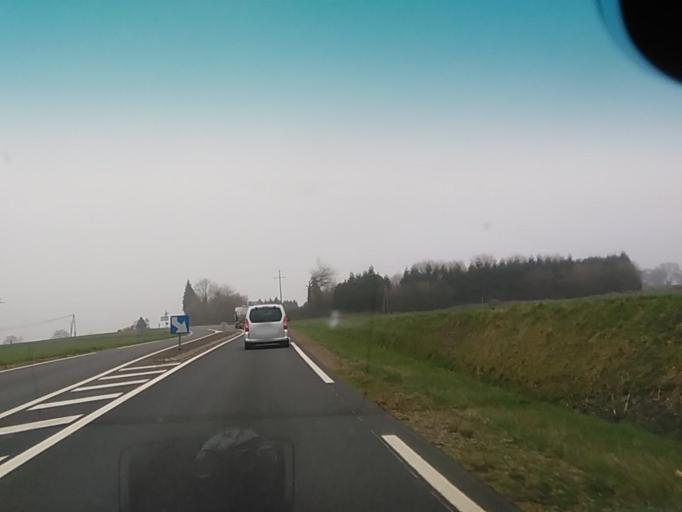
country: FR
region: Lower Normandy
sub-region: Departement de l'Orne
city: Magny-le-Desert
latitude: 48.6269
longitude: -0.2655
